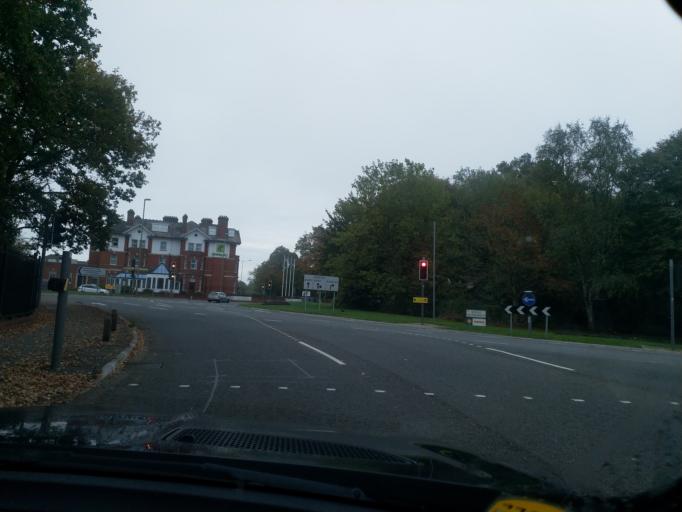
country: GB
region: England
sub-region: Hampshire
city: Farnborough
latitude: 51.2739
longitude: -0.7578
